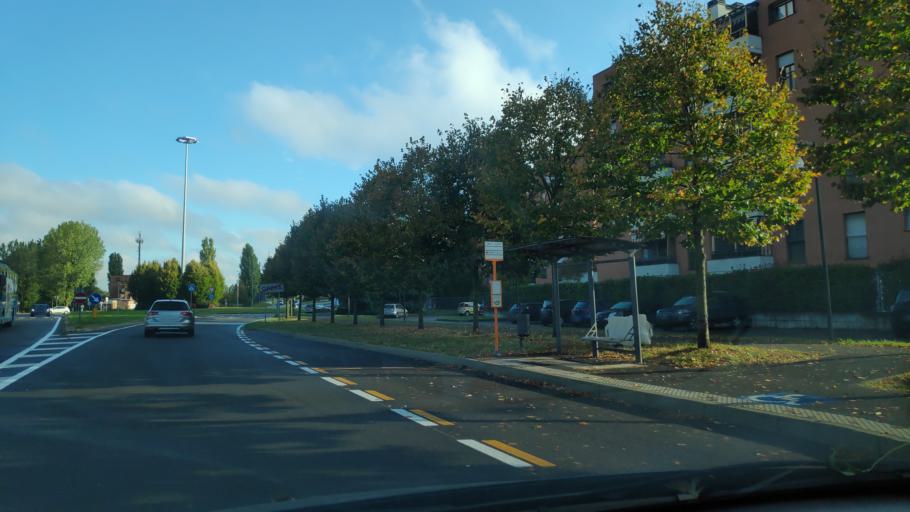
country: IT
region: Lombardy
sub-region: Citta metropolitana di Milano
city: Opera
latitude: 45.3816
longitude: 9.2131
